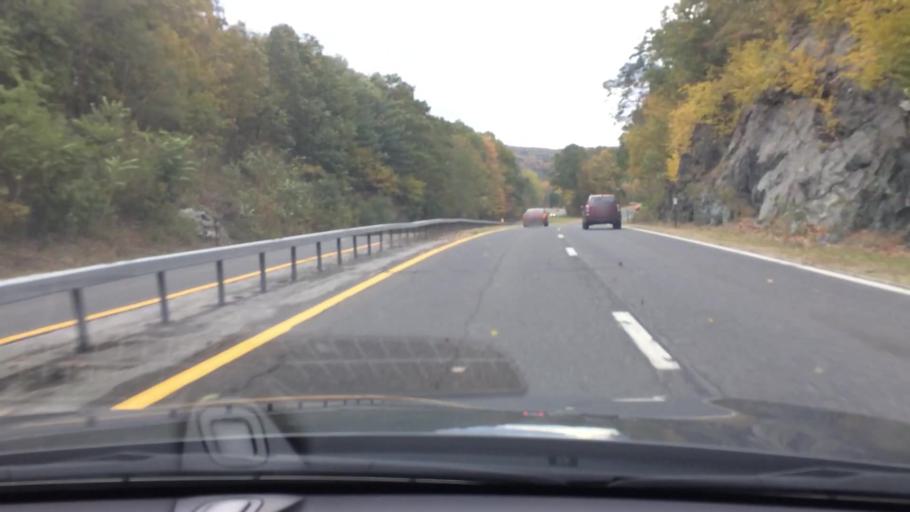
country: US
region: New York
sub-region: Dutchess County
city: Pleasant Valley
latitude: 41.7825
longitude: -73.7692
